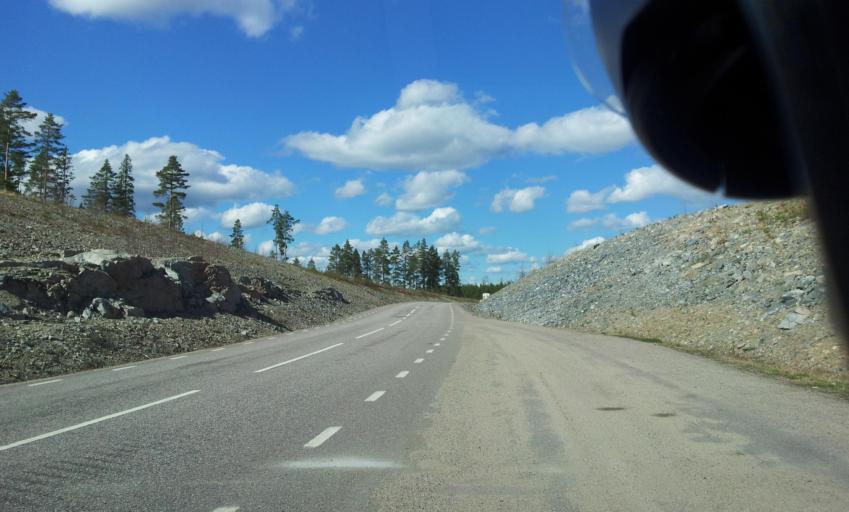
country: SE
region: Gaevleborg
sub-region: Ovanakers Kommun
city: Edsbyn
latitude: 61.2331
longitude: 15.8834
